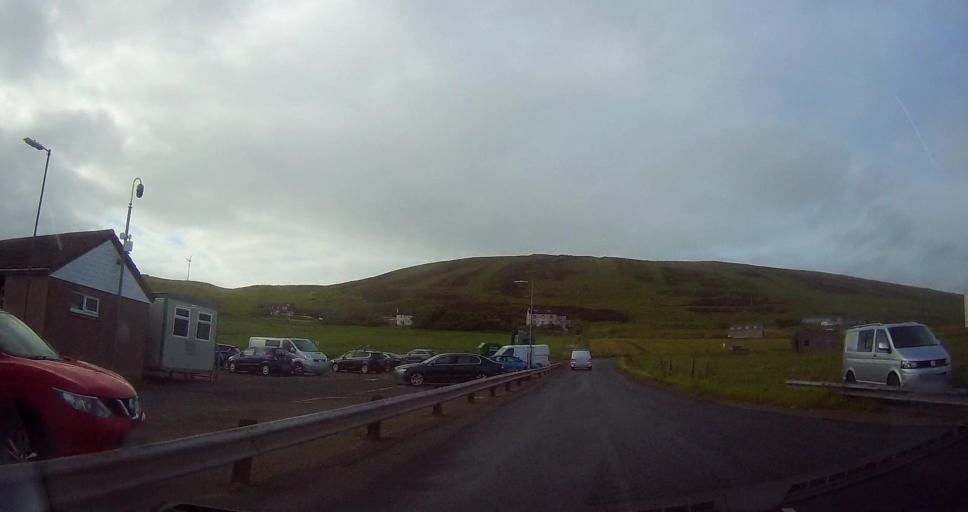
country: GB
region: Scotland
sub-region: Orkney Islands
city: Stromness
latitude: 58.9185
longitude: -3.1845
